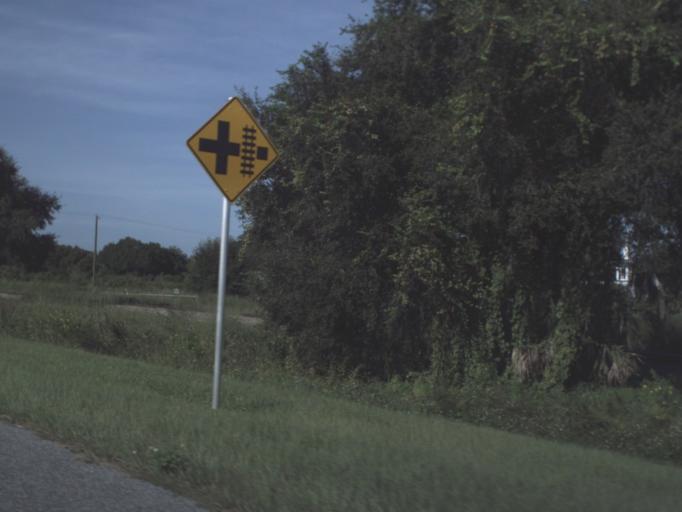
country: US
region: Florida
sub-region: DeSoto County
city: Nocatee
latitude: 27.0857
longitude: -81.9542
